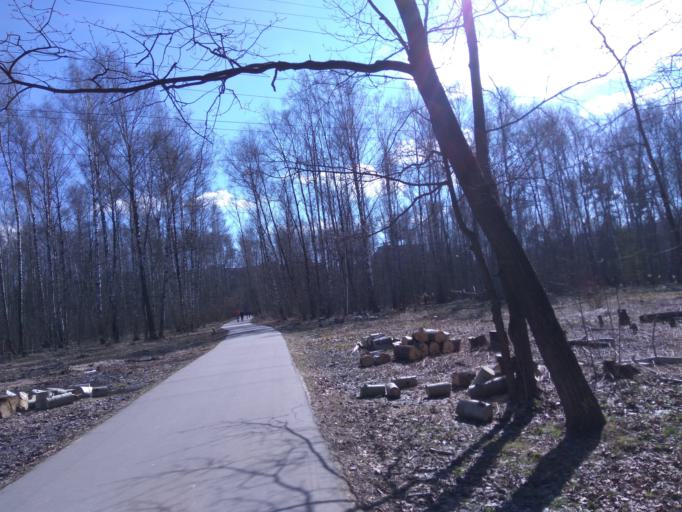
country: RU
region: Moscow
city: Ivanovskoye
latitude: 55.7850
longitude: 37.8317
